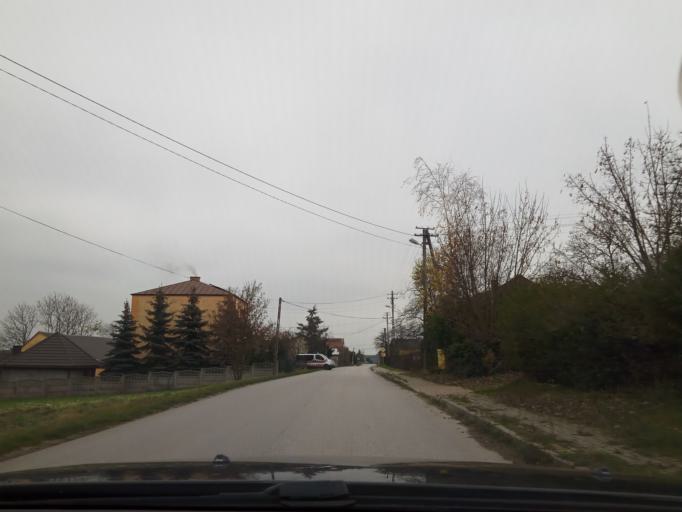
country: PL
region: Swietokrzyskie
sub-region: Powiat jedrzejowski
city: Imielno
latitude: 50.5870
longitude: 20.4442
